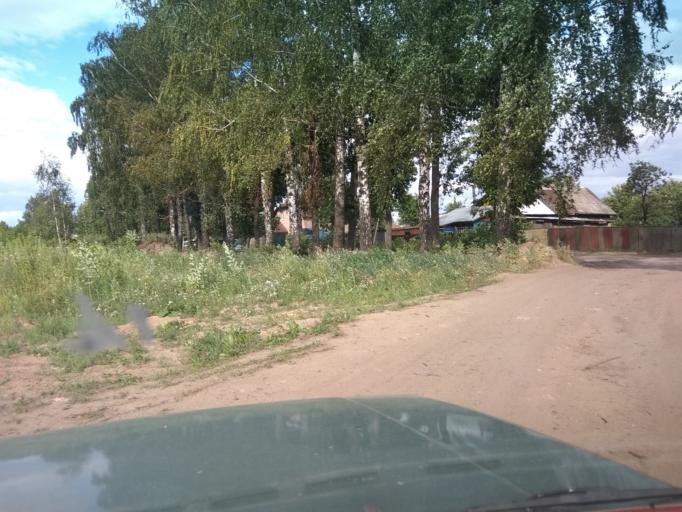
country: BY
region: Mogilev
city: Mahilyow
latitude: 53.9209
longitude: 30.3552
